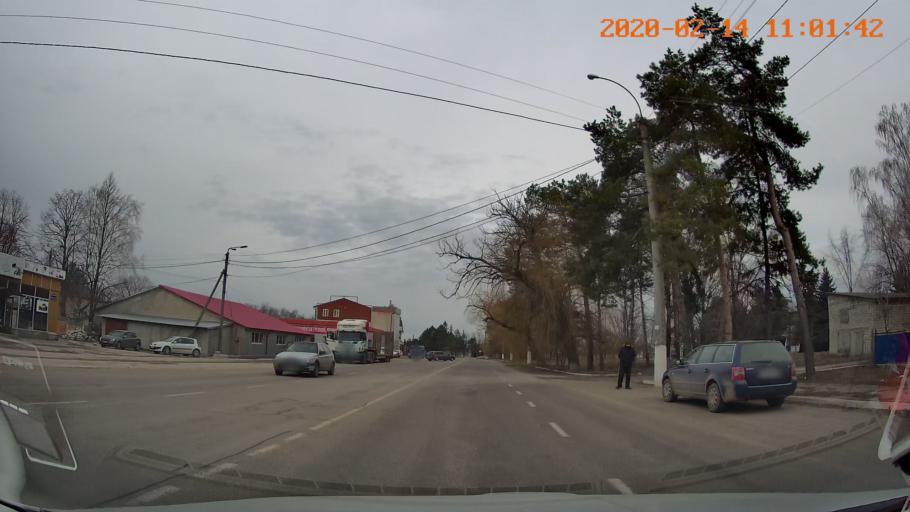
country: MD
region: Raionul Edinet
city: Edinet
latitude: 48.1614
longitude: 27.3268
